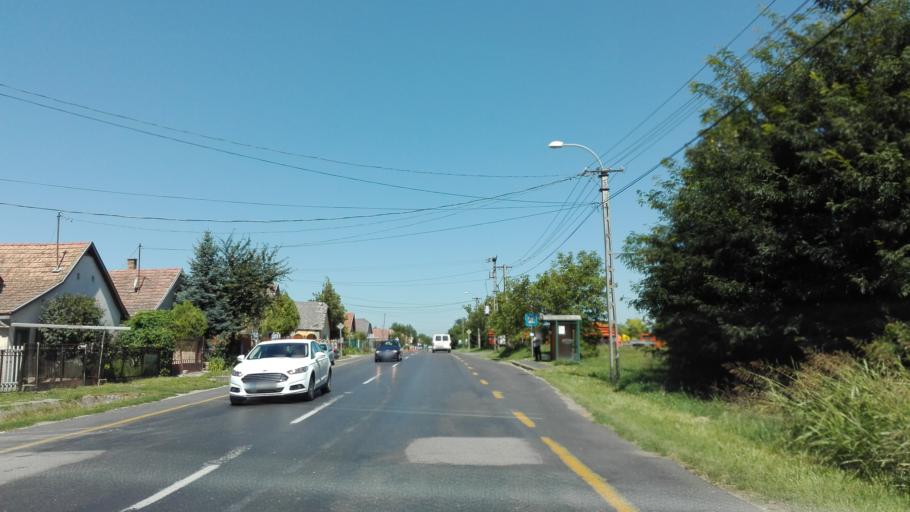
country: HU
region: Fejer
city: Mezoszilas
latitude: 46.7798
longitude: 18.5110
